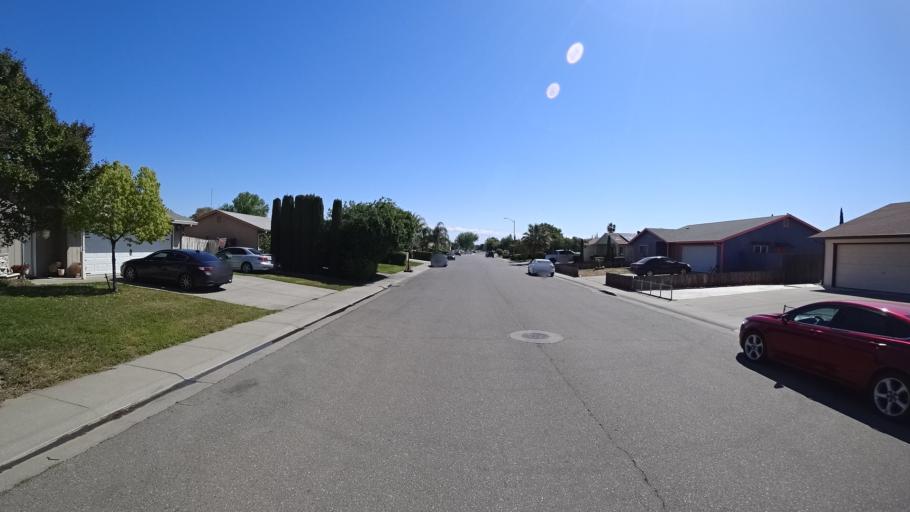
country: US
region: California
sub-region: Glenn County
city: Orland
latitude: 39.7571
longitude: -122.2036
